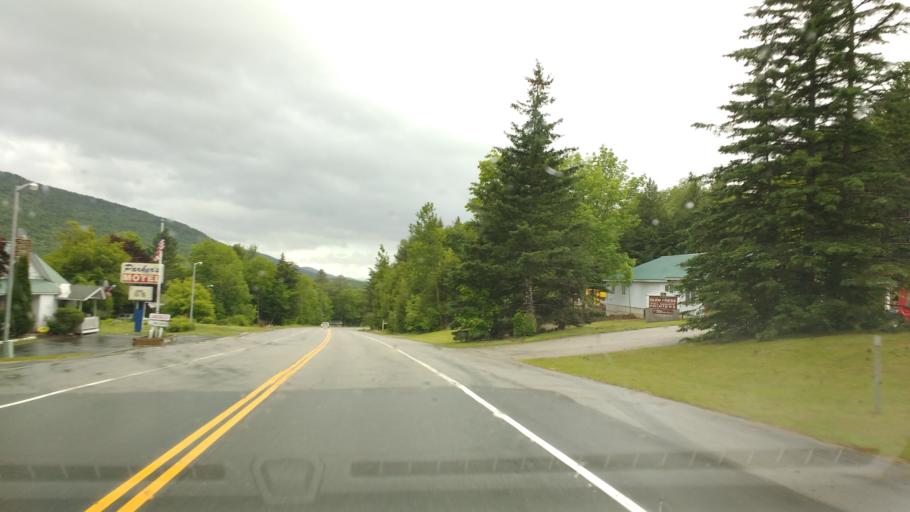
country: US
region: New Hampshire
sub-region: Grafton County
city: Woodstock
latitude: 44.0905
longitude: -71.6838
